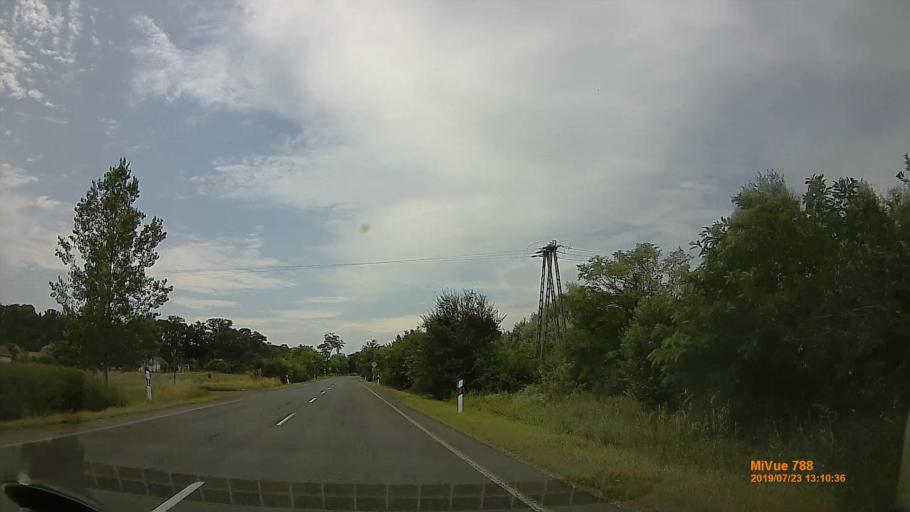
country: HU
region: Szabolcs-Szatmar-Bereg
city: Tiszavasvari
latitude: 47.9259
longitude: 21.2890
